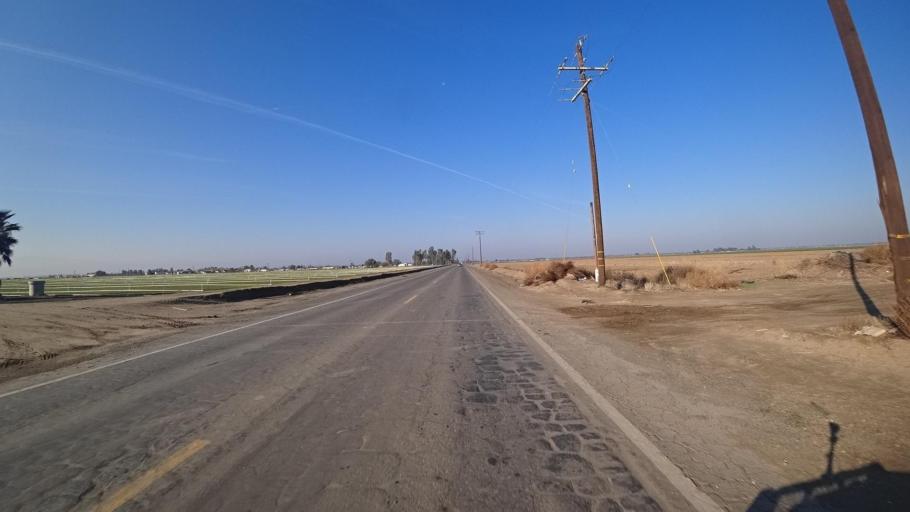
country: US
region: California
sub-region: Kern County
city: Lamont
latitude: 35.2526
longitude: -118.9496
